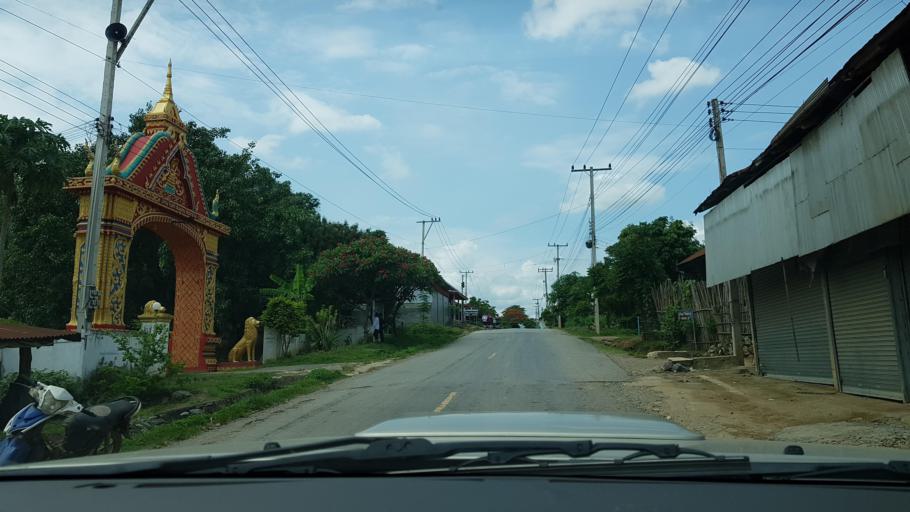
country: LA
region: Loungnamtha
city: Muang Nale
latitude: 20.1078
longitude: 101.4158
